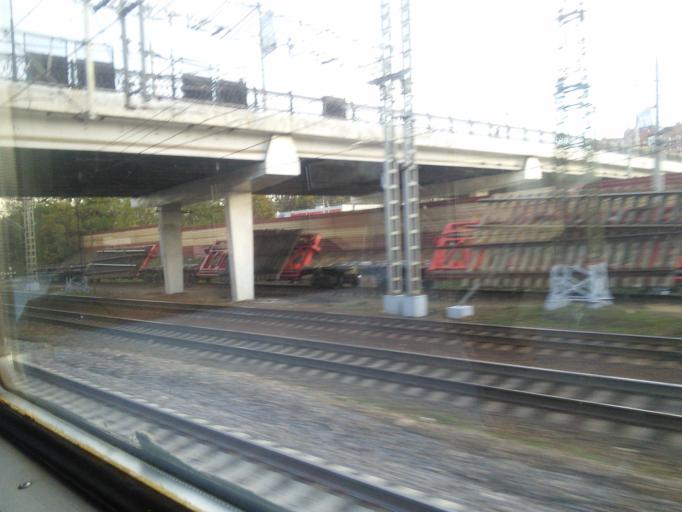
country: RU
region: Moscow
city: Khimki
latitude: 55.8962
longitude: 37.4474
